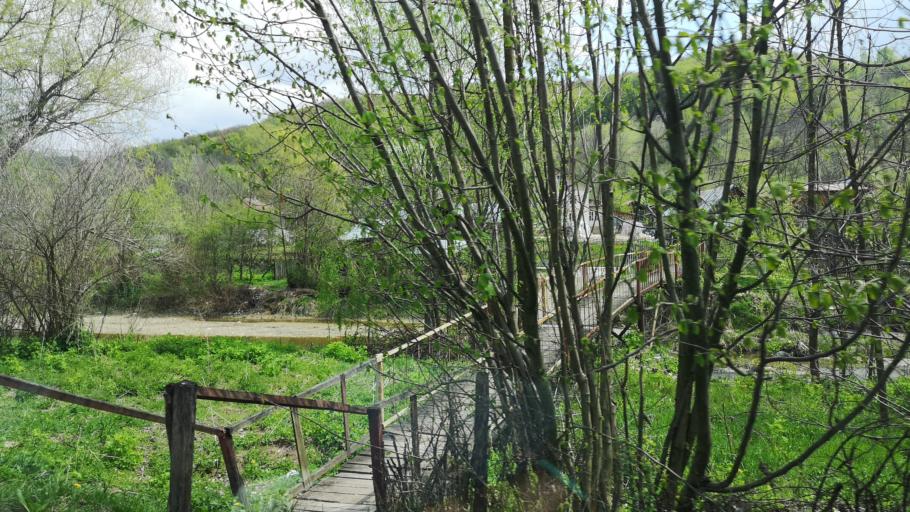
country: RO
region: Prahova
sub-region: Comuna Soimari
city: Soimari
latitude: 45.1662
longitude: 26.2107
